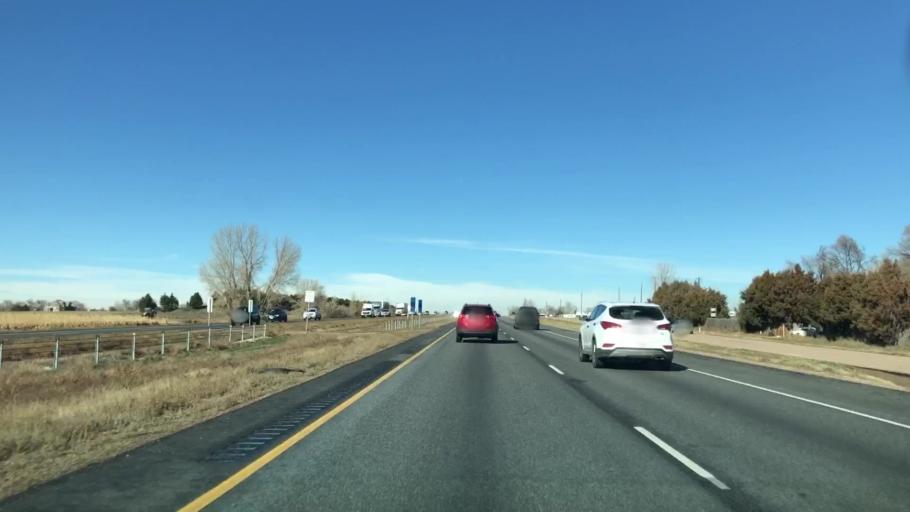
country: US
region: Colorado
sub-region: Weld County
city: Mead
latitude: 40.2463
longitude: -104.9801
